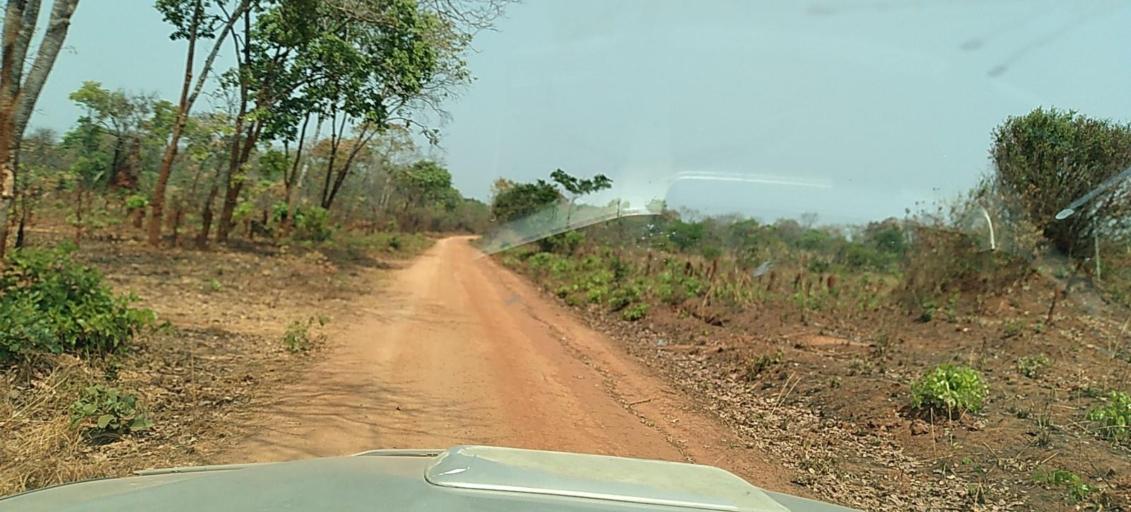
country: ZM
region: North-Western
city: Kasempa
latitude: -13.6830
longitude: 26.3166
